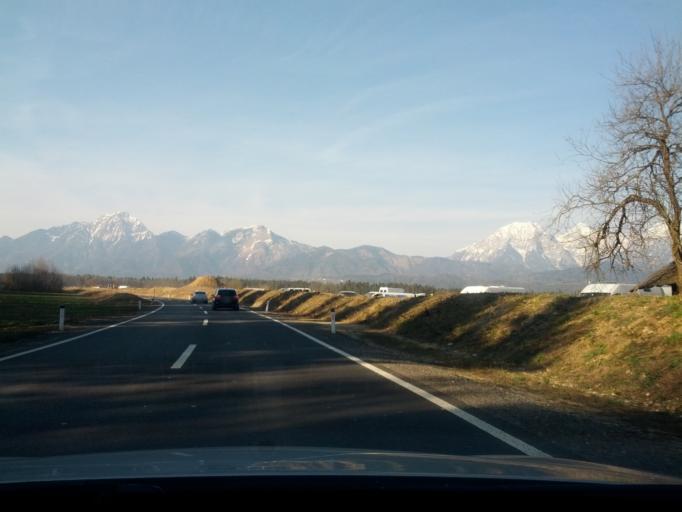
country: SI
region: Sencur
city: Sencur
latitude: 46.2249
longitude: 14.4421
